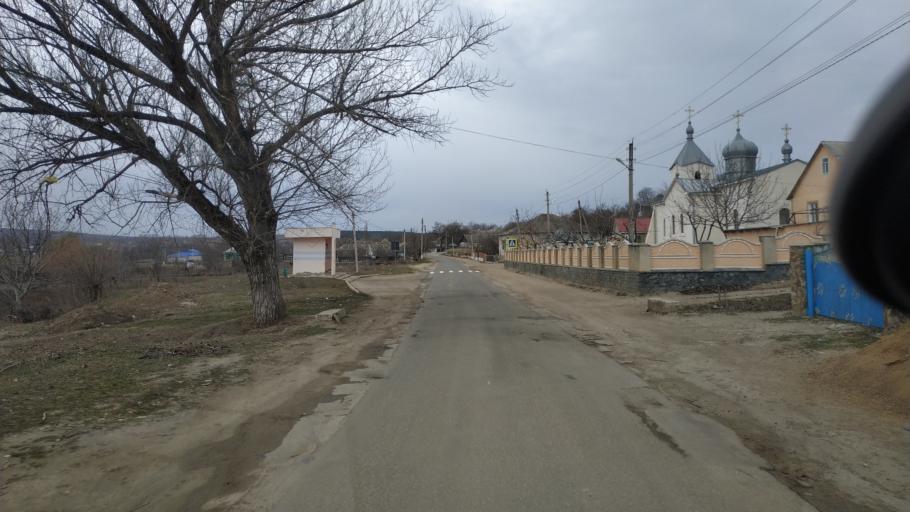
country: MD
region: Telenesti
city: Cocieri
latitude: 47.2680
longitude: 29.0695
